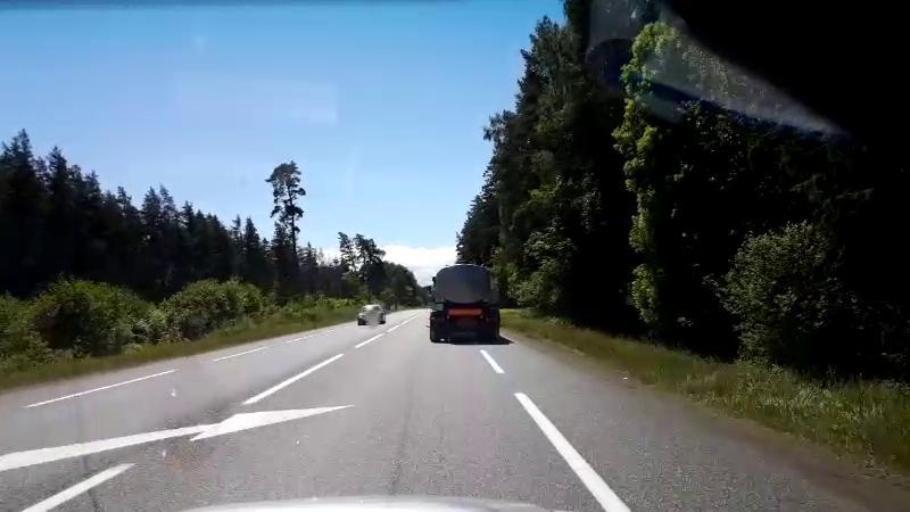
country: LV
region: Saulkrastu
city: Saulkrasti
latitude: 57.3903
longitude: 24.4286
